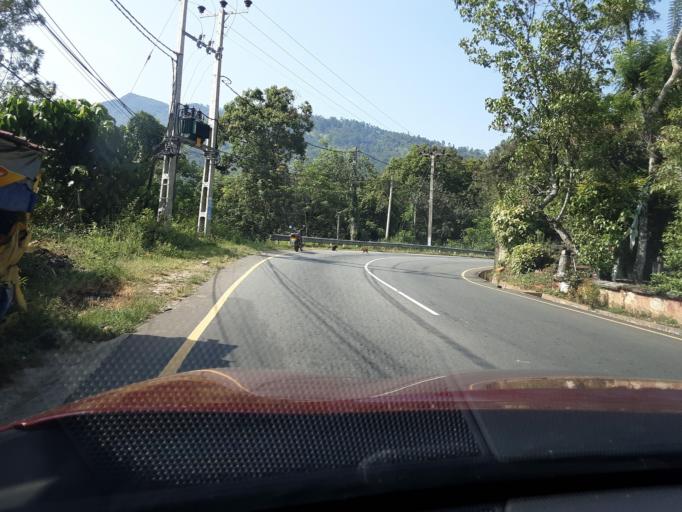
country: LK
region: Uva
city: Badulla
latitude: 6.9721
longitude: 81.0863
